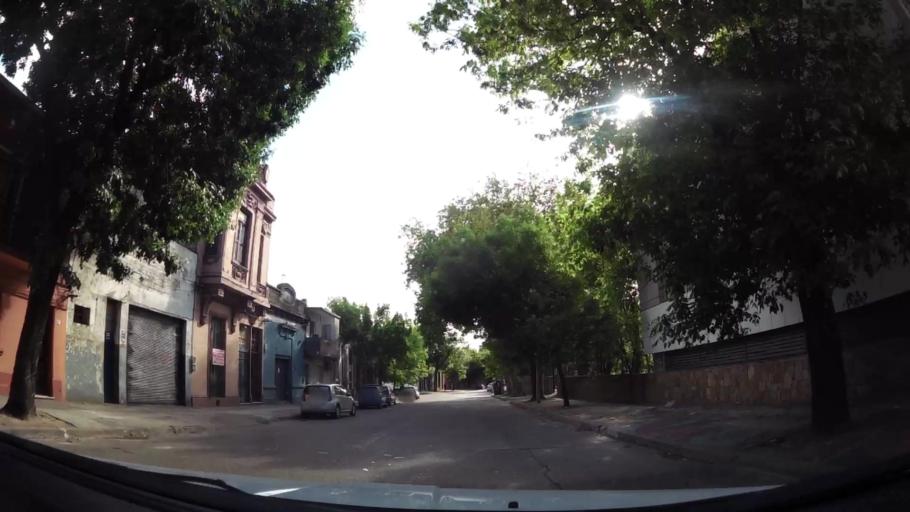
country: UY
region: Montevideo
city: Montevideo
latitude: -34.8910
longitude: -56.1830
